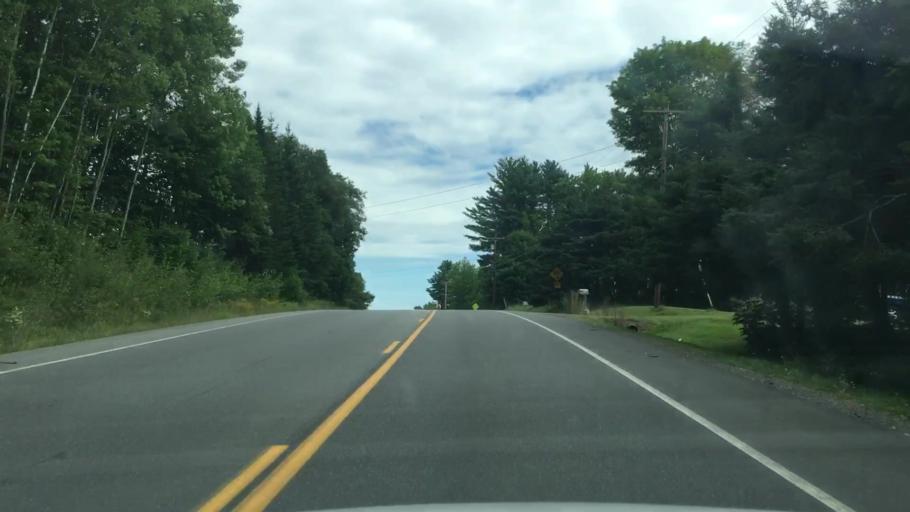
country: US
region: Maine
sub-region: Piscataquis County
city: Milo
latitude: 45.2364
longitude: -69.0559
